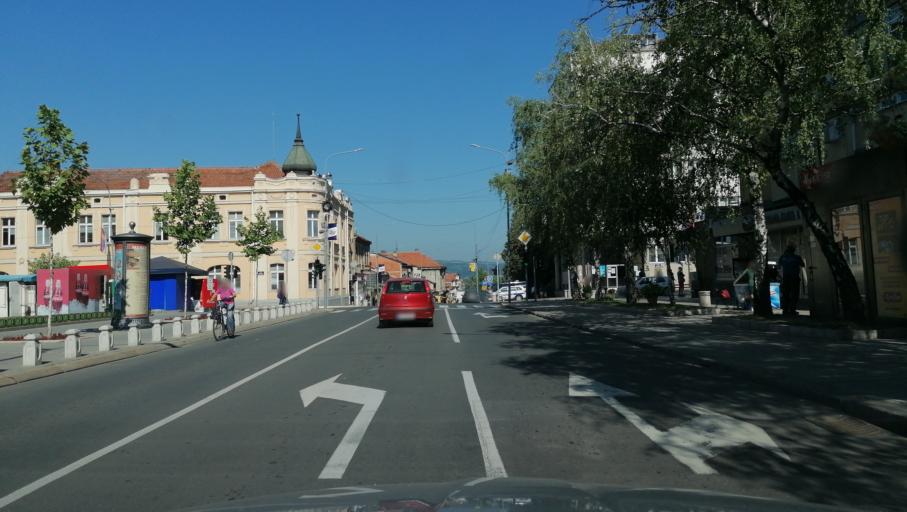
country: RS
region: Central Serbia
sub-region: Rasinski Okrug
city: Krusevac
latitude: 43.5836
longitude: 21.3249
